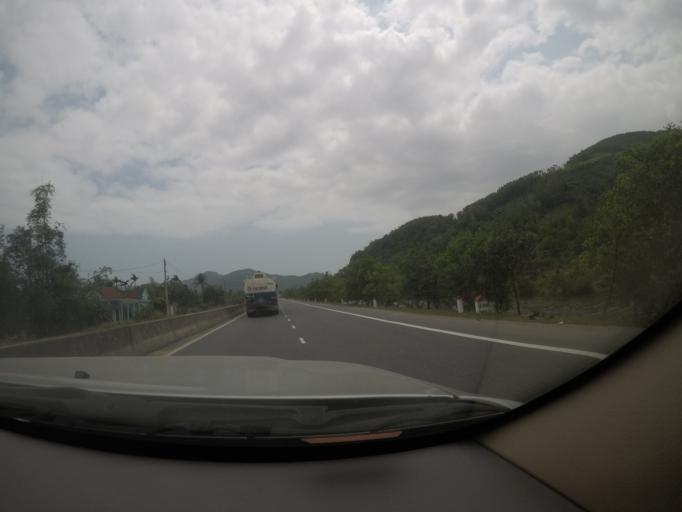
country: VN
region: Thua Thien-Hue
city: Phu Loc
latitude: 16.2706
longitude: 108.0110
